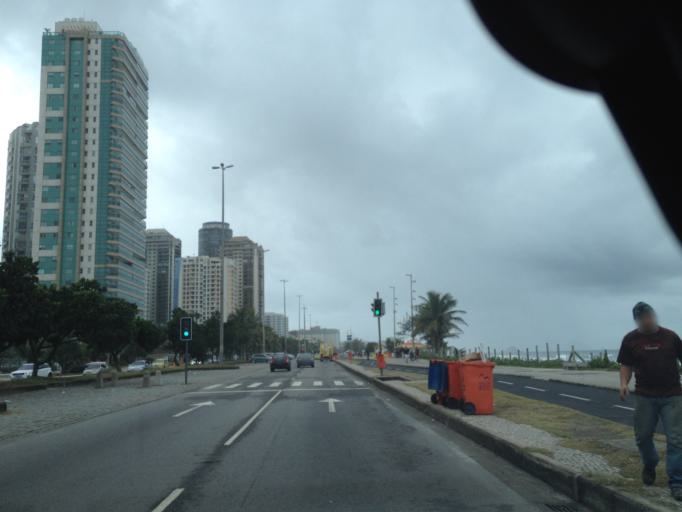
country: BR
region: Rio de Janeiro
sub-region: Rio De Janeiro
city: Rio de Janeiro
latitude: -23.0107
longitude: -43.3345
